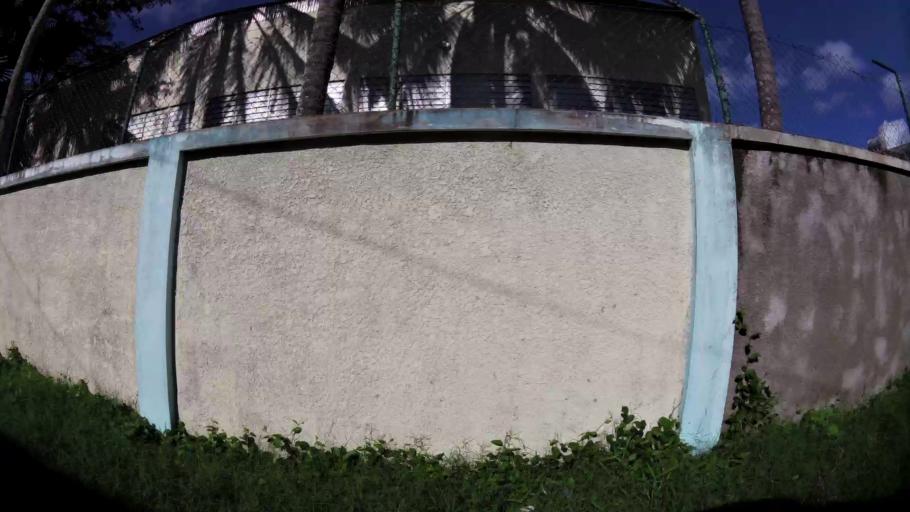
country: MU
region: Grand Port
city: Mahebourg
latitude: -20.4127
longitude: 57.7103
